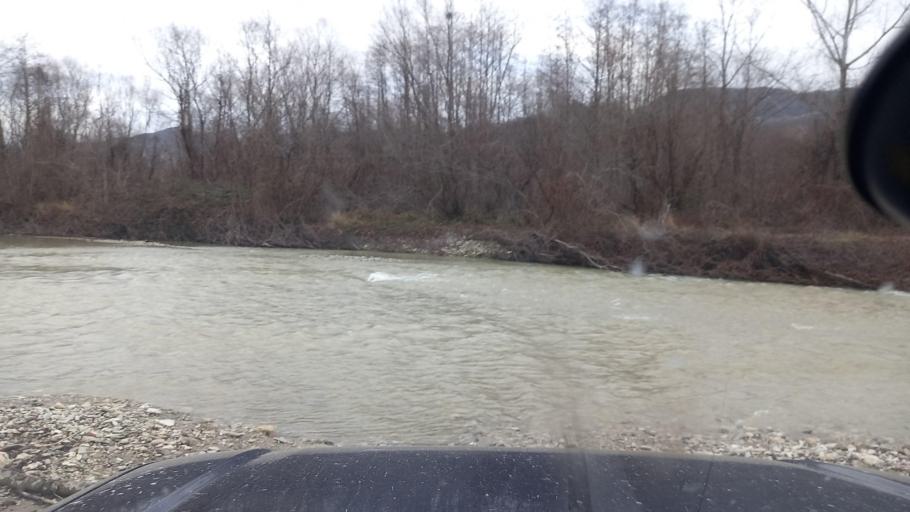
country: RU
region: Krasnodarskiy
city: Pshada
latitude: 44.4923
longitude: 38.4176
